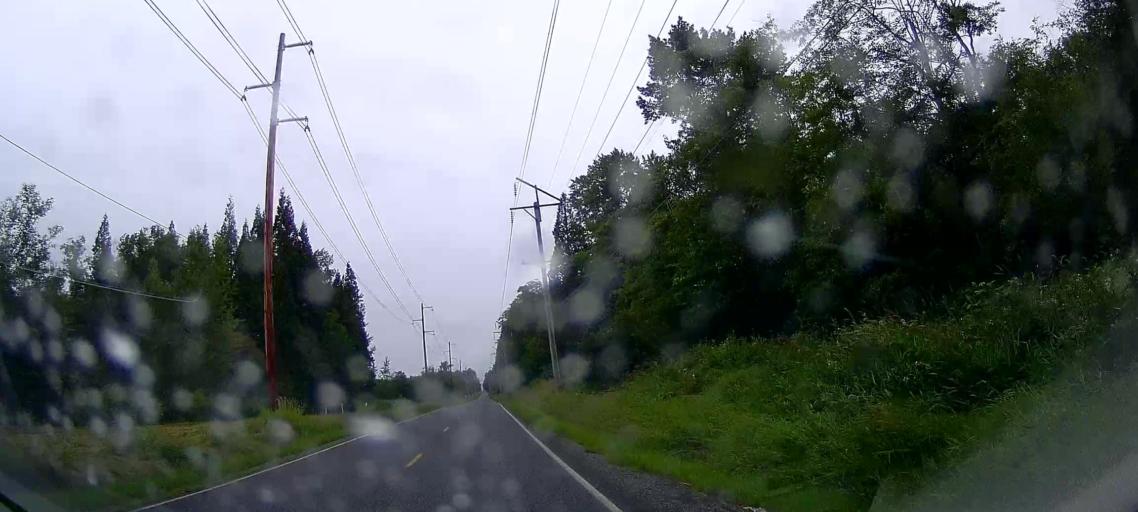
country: US
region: Washington
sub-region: Whatcom County
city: Birch Bay
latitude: 48.8684
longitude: -122.7044
